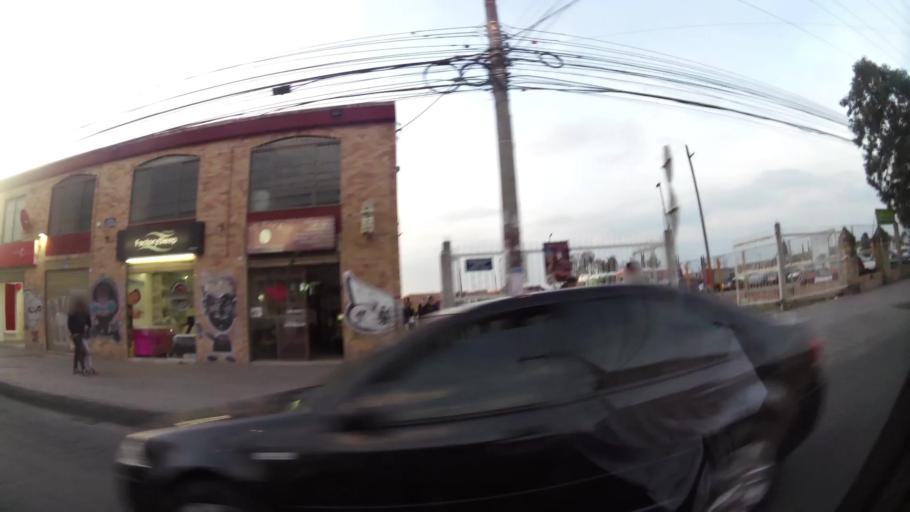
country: CO
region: Cundinamarca
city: Funza
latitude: 4.7136
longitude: -74.2183
